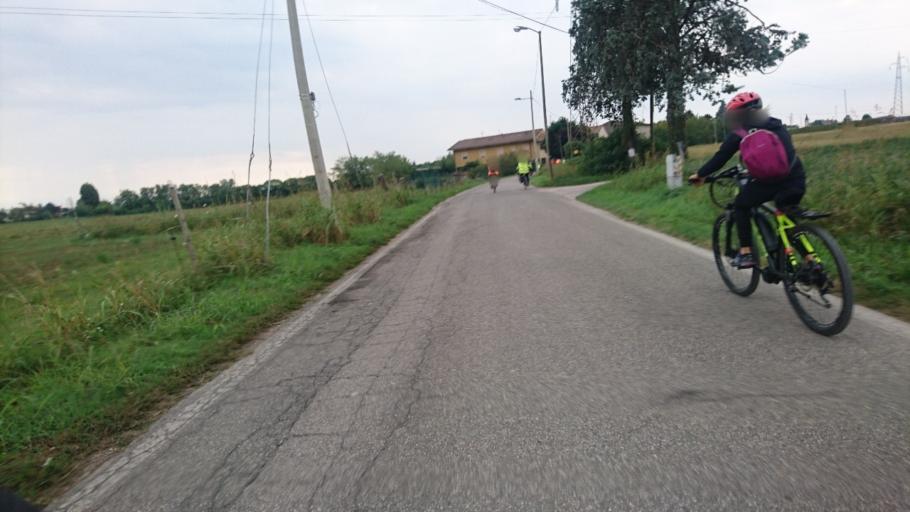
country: IT
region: Veneto
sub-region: Provincia di Verona
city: San Martino Buon Albergo
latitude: 45.4195
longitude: 11.0567
